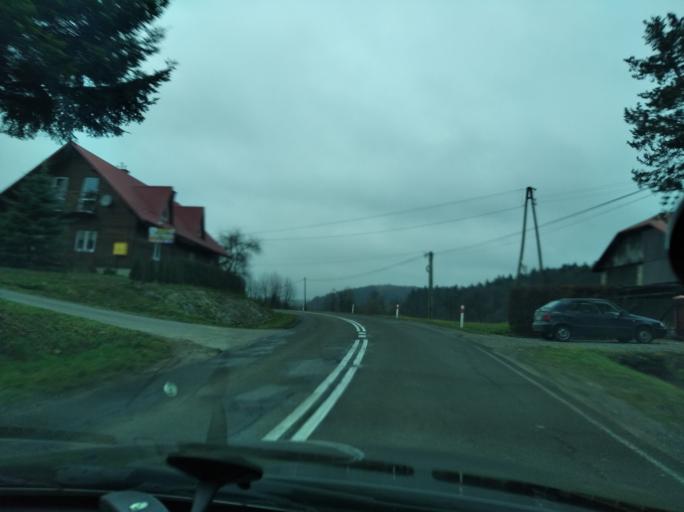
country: PL
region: Subcarpathian Voivodeship
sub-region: Powiat rzeszowski
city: Dynow
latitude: 49.8563
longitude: 22.2500
